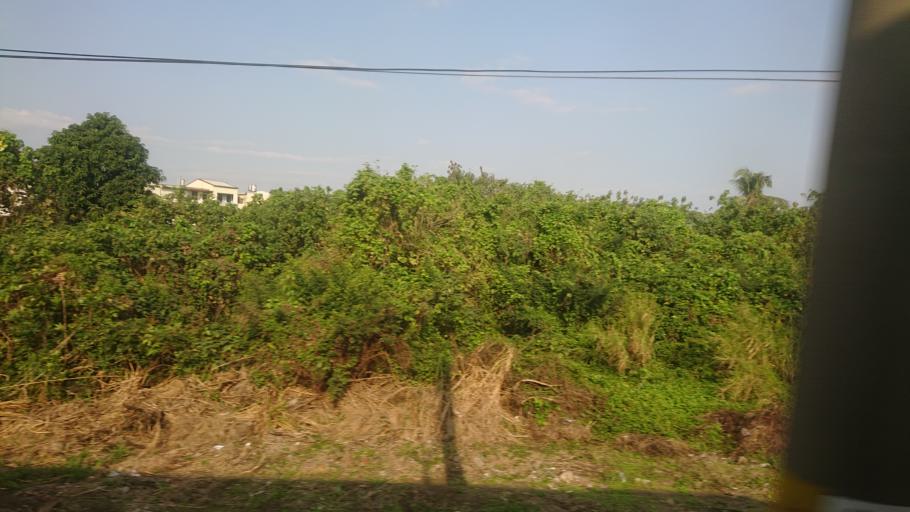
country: TW
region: Taiwan
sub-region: Chiayi
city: Jiayi Shi
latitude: 23.5914
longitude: 120.4466
